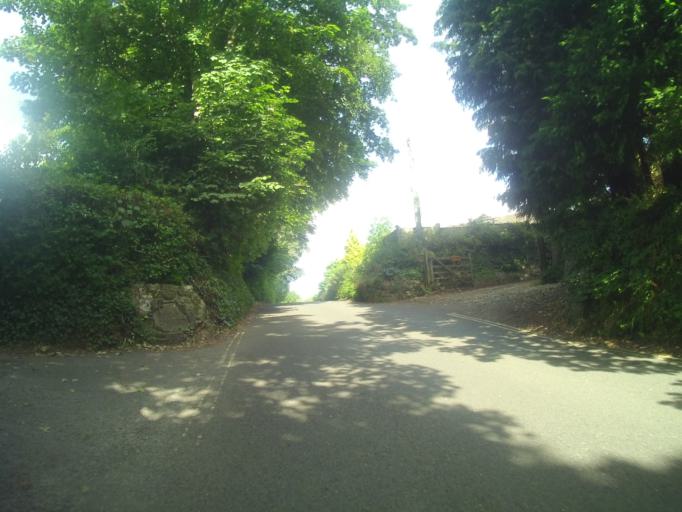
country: GB
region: England
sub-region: Devon
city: Totnes
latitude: 50.4353
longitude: -3.6974
